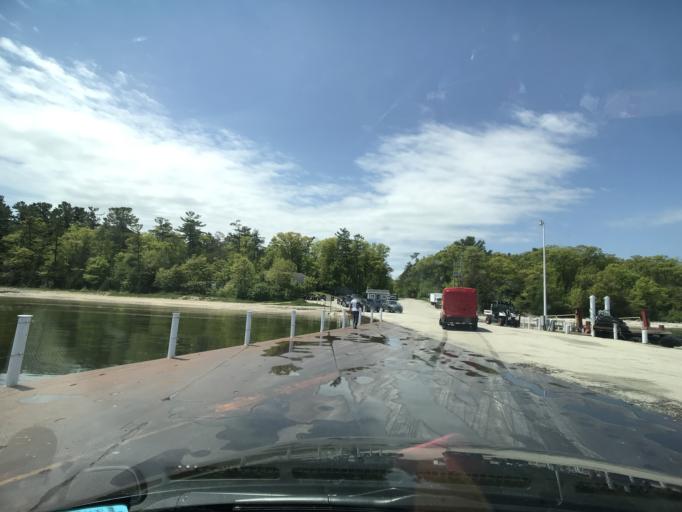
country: US
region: Michigan
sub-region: Delta County
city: Escanaba
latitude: 45.2908
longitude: -86.9767
